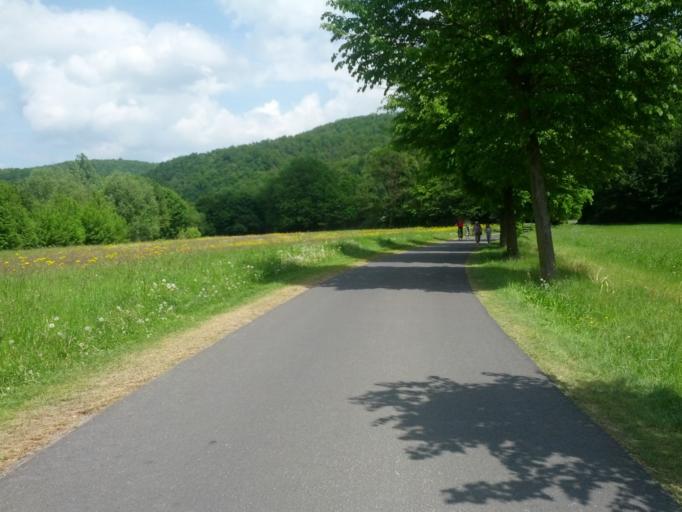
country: DE
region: Thuringia
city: Frankenroda
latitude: 51.1011
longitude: 10.2866
